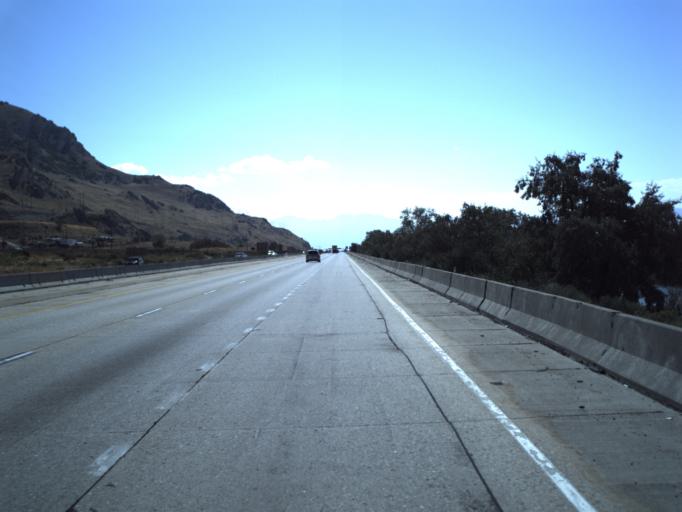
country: US
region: Utah
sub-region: Tooele County
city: Stansbury park
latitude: 40.7202
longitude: -112.2315
